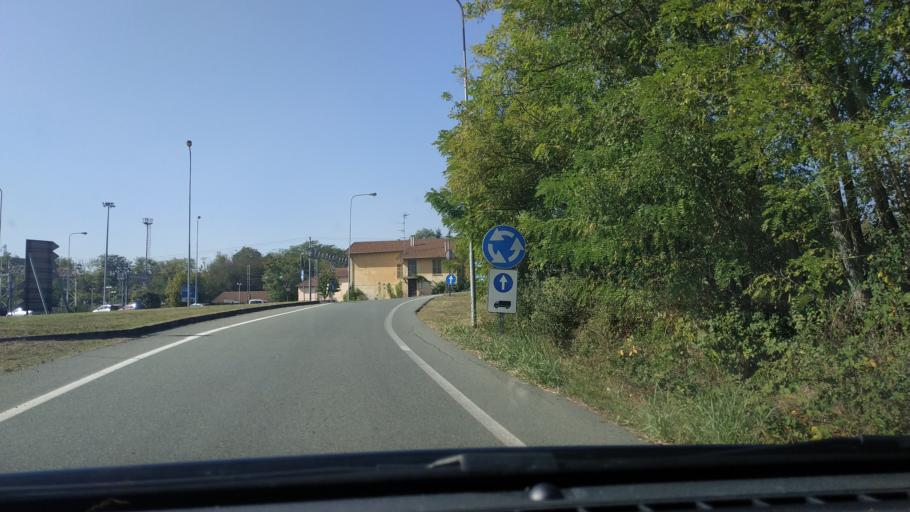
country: IT
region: Piedmont
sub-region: Provincia di Alessandria
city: Valenza
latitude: 45.0250
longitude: 8.6267
